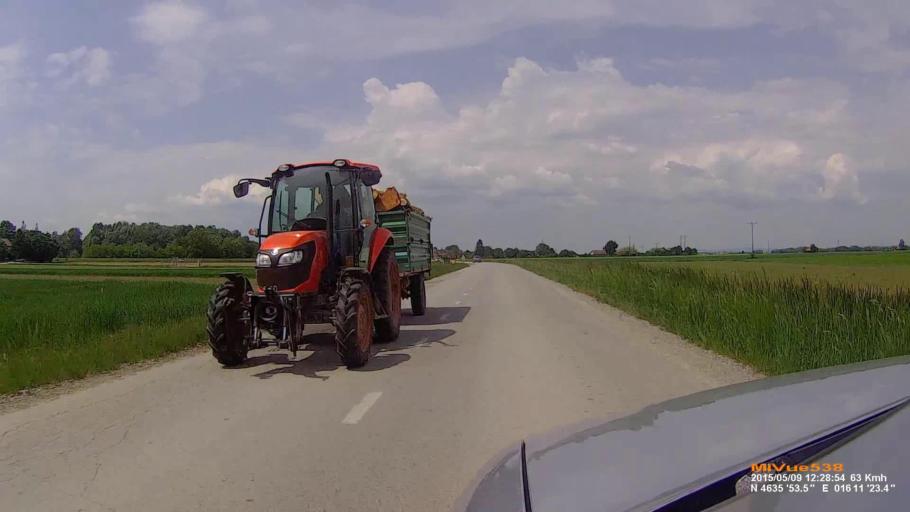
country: SI
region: Verzej
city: Verzej
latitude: 46.5983
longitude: 16.1896
